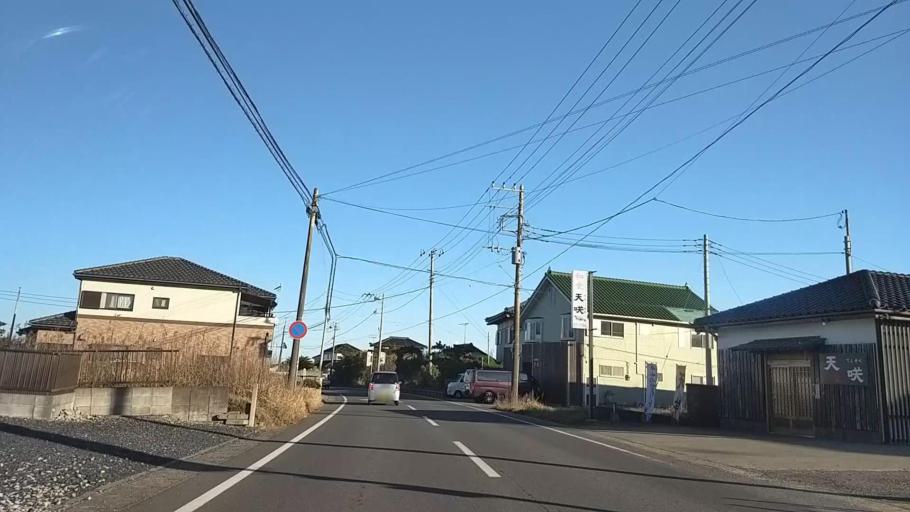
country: JP
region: Chiba
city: Asahi
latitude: 35.7010
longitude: 140.6895
